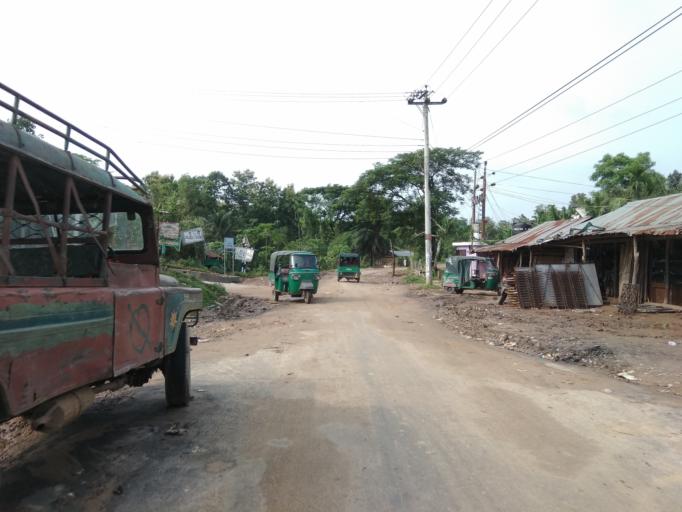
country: BD
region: Chittagong
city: Khagrachhari
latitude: 23.0130
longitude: 92.0142
